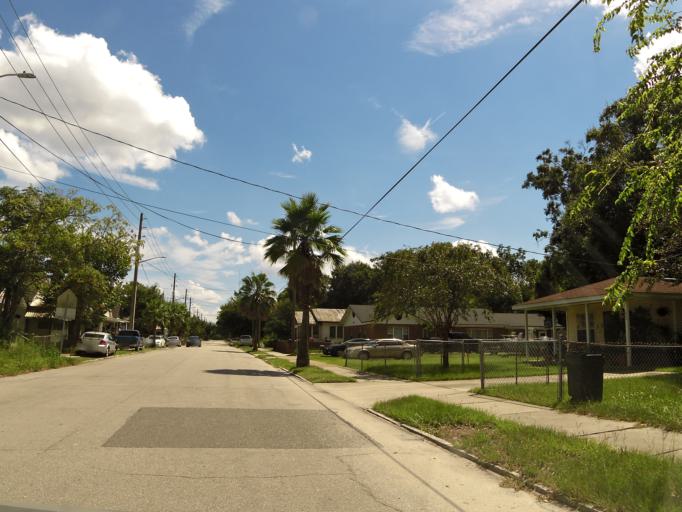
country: US
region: Florida
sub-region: Duval County
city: Jacksonville
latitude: 30.3417
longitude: -81.6423
